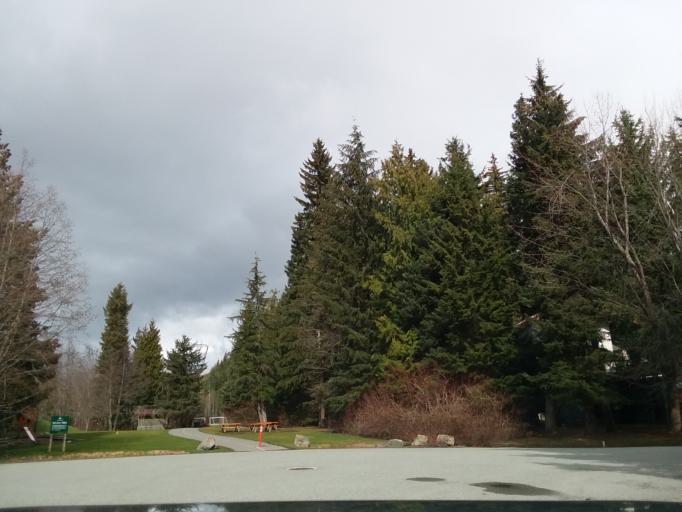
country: CA
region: British Columbia
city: Whistler
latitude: 50.1301
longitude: -122.9657
